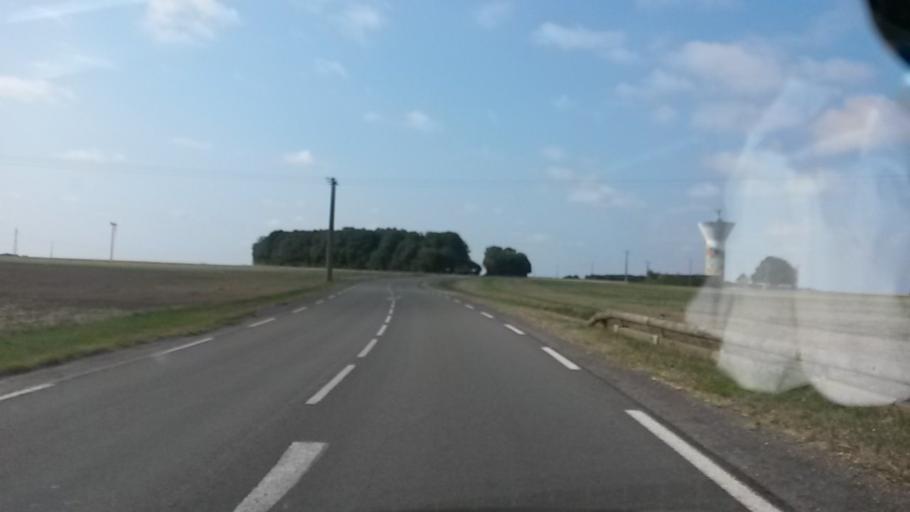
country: FR
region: Haute-Normandie
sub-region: Departement de l'Eure
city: Damville
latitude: 48.8586
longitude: 1.0644
